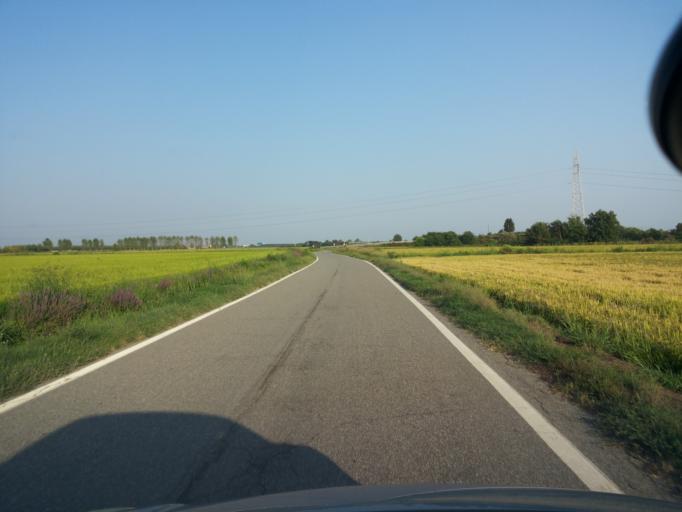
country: IT
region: Piedmont
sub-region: Provincia di Vercelli
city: Lignana
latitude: 45.3021
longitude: 8.3484
